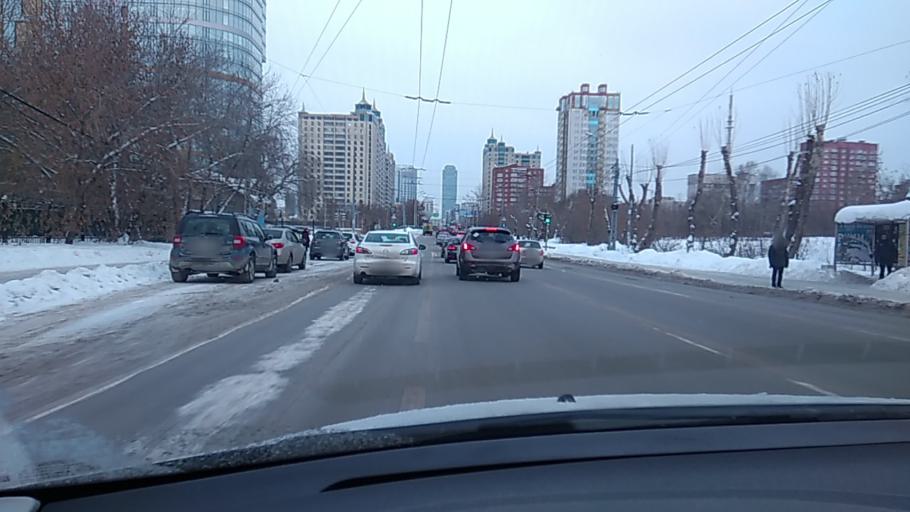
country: RU
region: Sverdlovsk
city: Yekaterinburg
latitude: 56.8184
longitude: 60.6200
